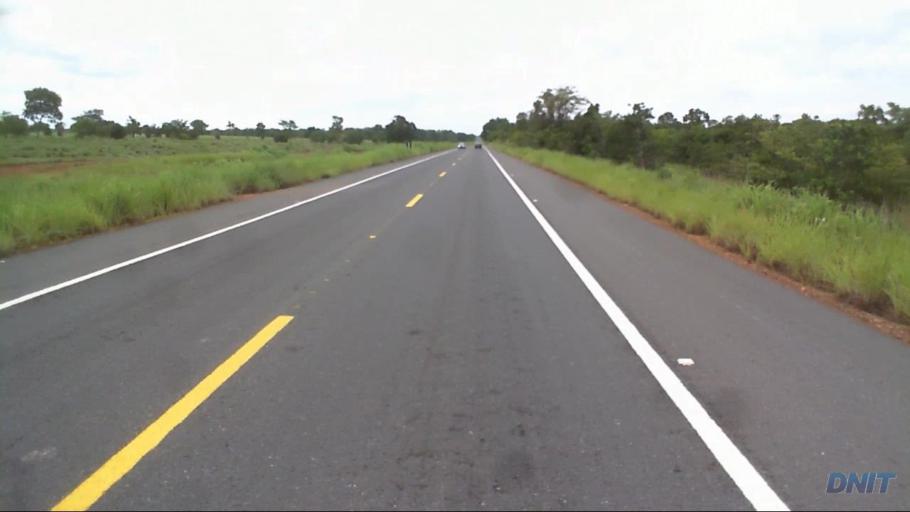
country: BR
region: Goias
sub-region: Sao Miguel Do Araguaia
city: Sao Miguel do Araguaia
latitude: -13.2647
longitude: -50.5129
